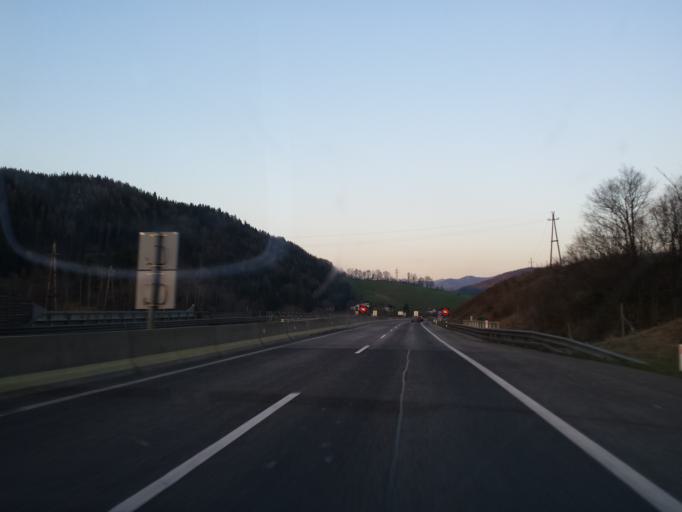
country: AT
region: Styria
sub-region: Politischer Bezirk Bruck-Muerzzuschlag
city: Muerzzuschlag
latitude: 47.6031
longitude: 15.7039
